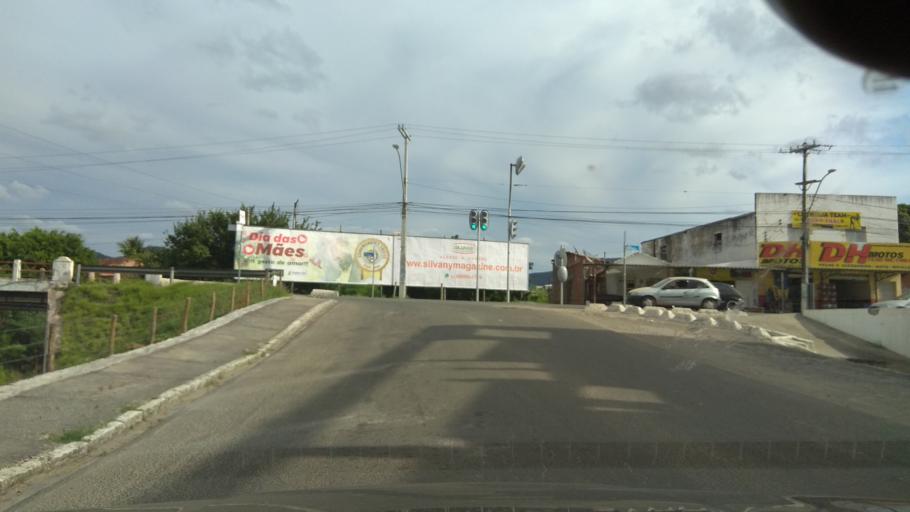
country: BR
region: Bahia
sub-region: Jequie
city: Jequie
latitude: -13.8652
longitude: -40.0779
